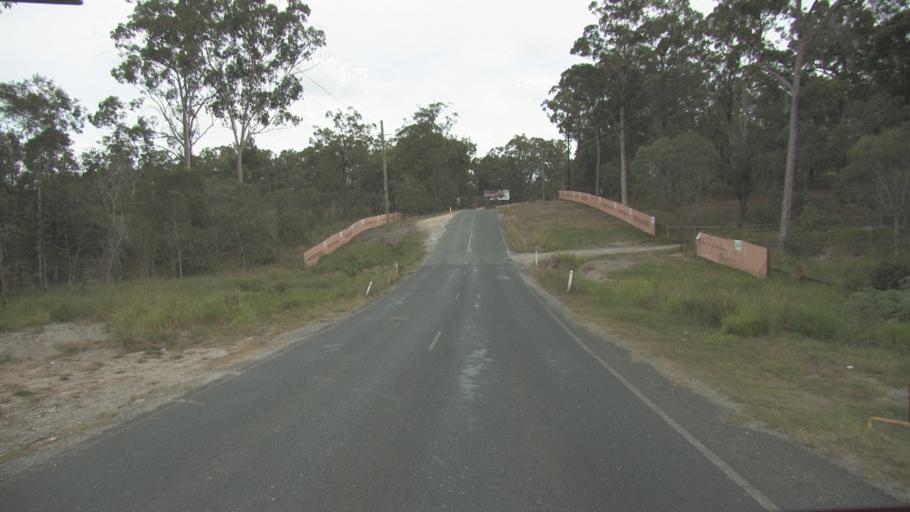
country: AU
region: Queensland
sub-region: Logan
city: Windaroo
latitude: -27.7326
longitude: 153.1628
